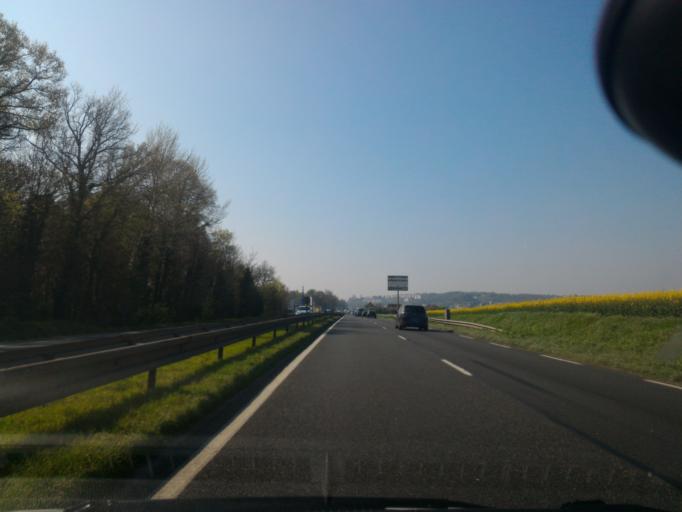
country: FR
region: Ile-de-France
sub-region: Departement de l'Essonne
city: Morigny-Champigny
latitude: 48.4640
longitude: 2.1807
